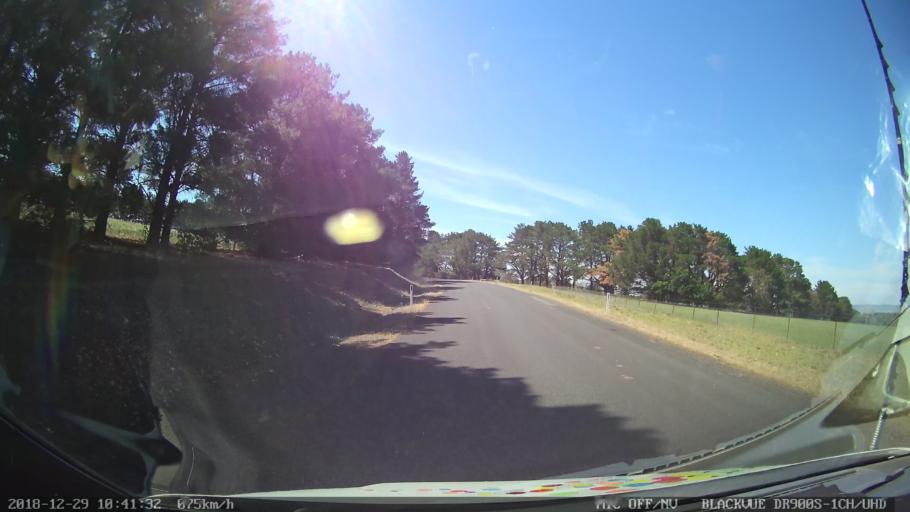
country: AU
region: New South Wales
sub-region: Palerang
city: Bungendore
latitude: -35.0265
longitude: 149.5214
